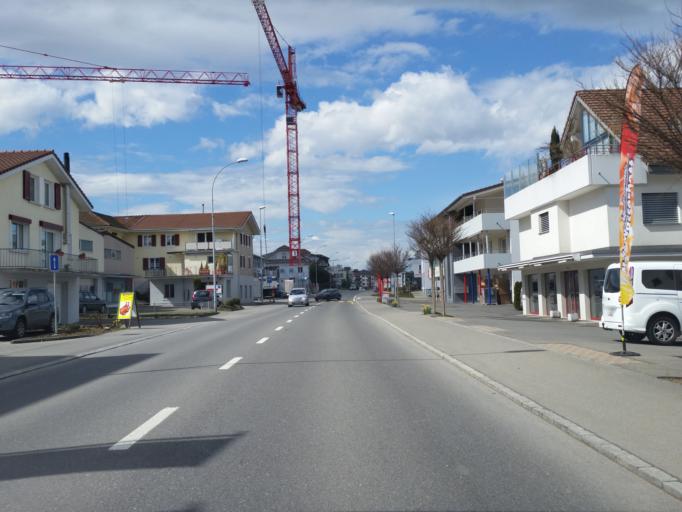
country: CH
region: Lucerne
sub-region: Sursee District
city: Nottwil
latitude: 47.1366
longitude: 8.1340
